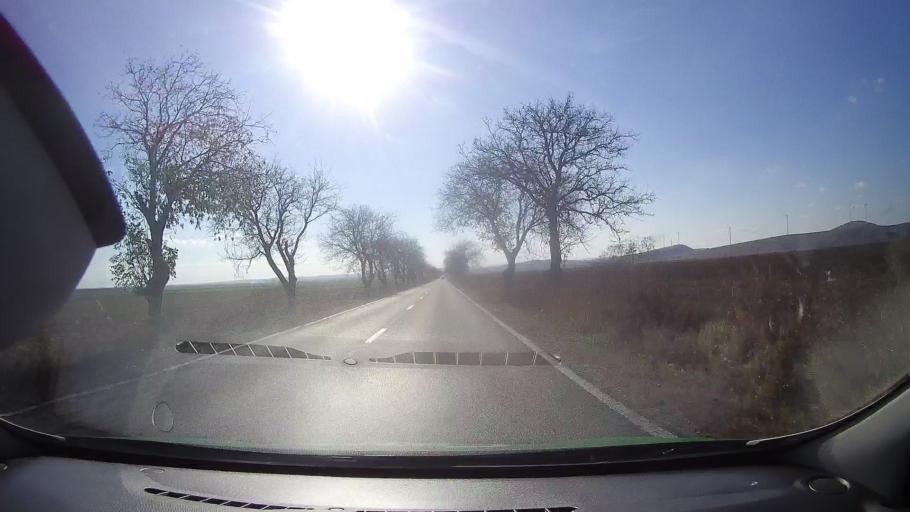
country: RO
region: Tulcea
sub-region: Comuna Ceamurlia de Jos
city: Ceamurlia de Jos
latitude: 44.7984
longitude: 28.6904
